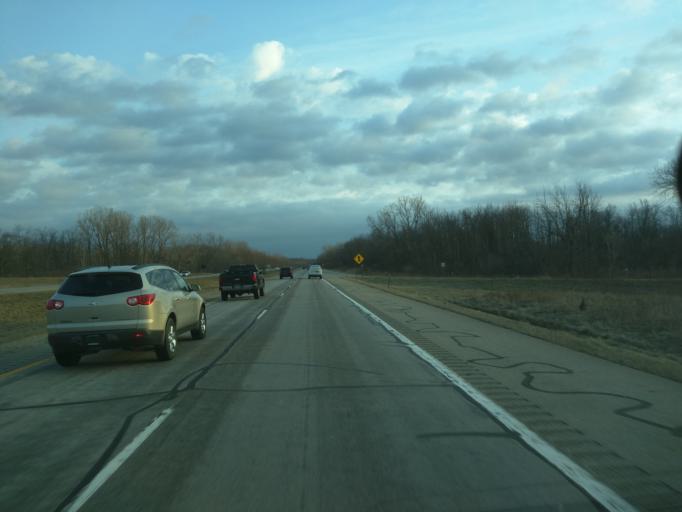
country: US
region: Michigan
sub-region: Ingham County
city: Holt
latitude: 42.6381
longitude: -84.4785
